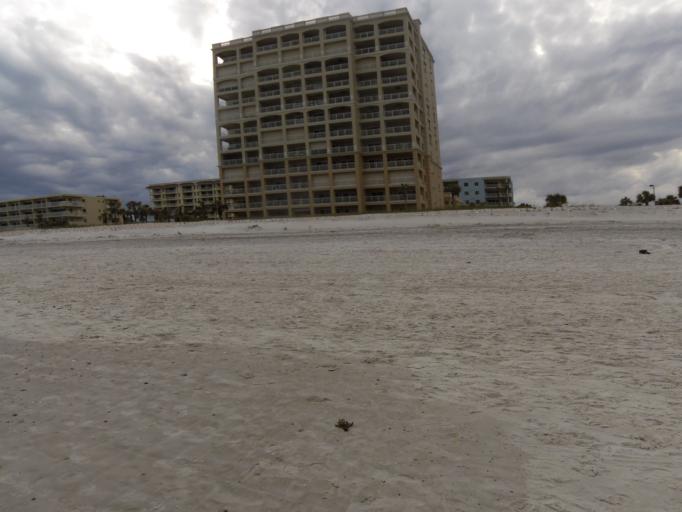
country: US
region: Florida
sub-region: Duval County
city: Jacksonville Beach
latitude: 30.3007
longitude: -81.3904
